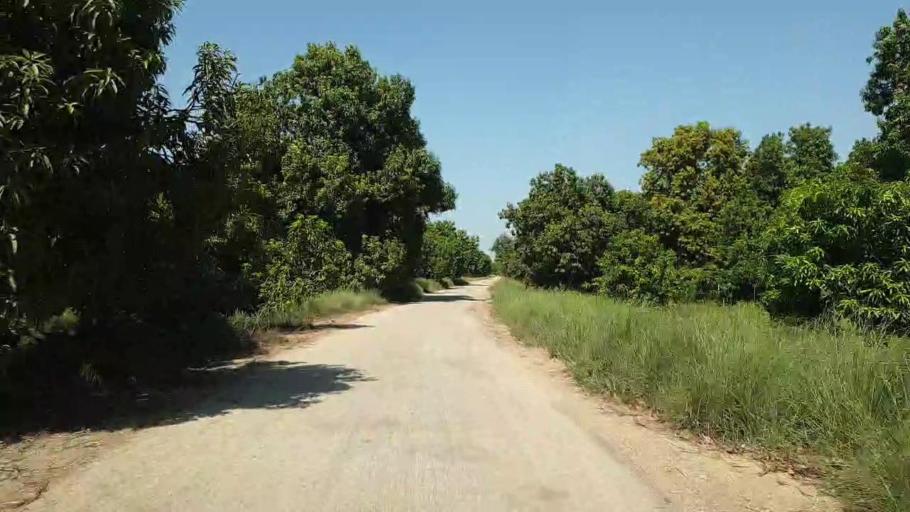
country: PK
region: Sindh
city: Tando Jam
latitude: 25.4313
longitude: 68.4597
